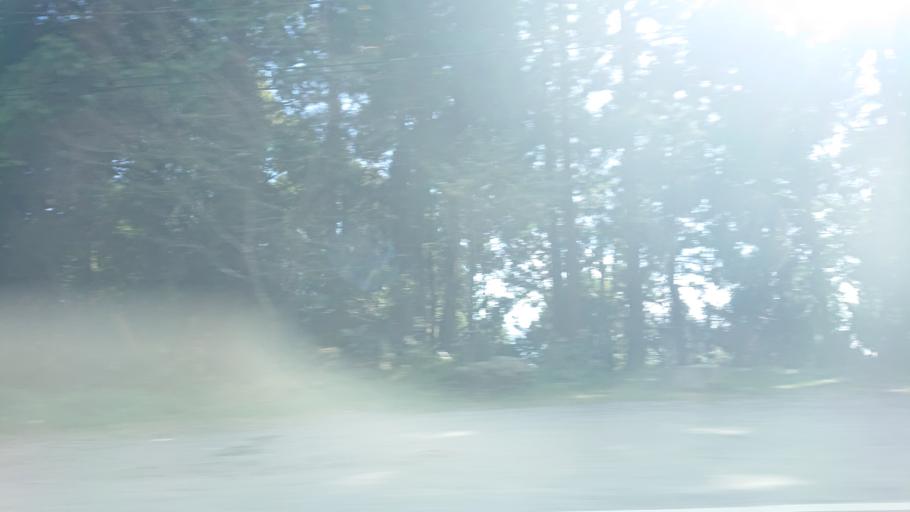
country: TW
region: Taiwan
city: Lugu
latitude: 23.5035
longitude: 120.8066
